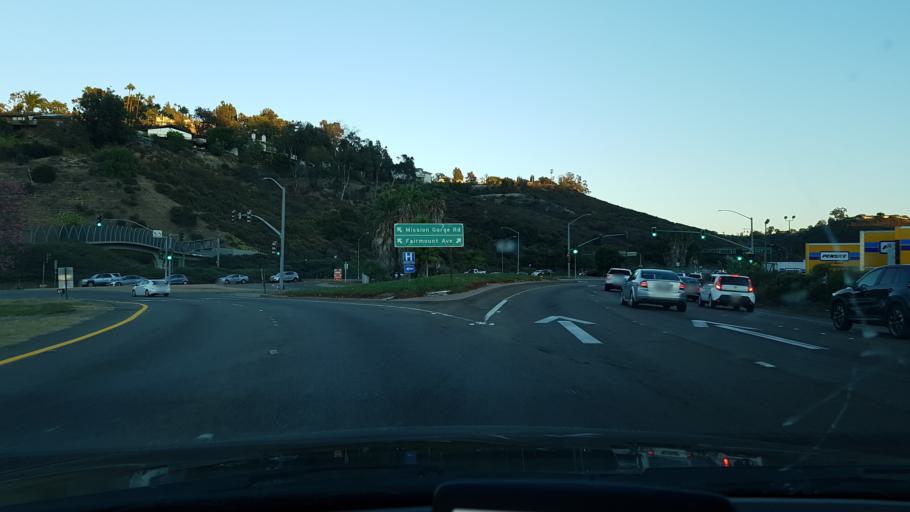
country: US
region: California
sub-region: San Diego County
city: Lemon Grove
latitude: 32.7780
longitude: -117.1017
